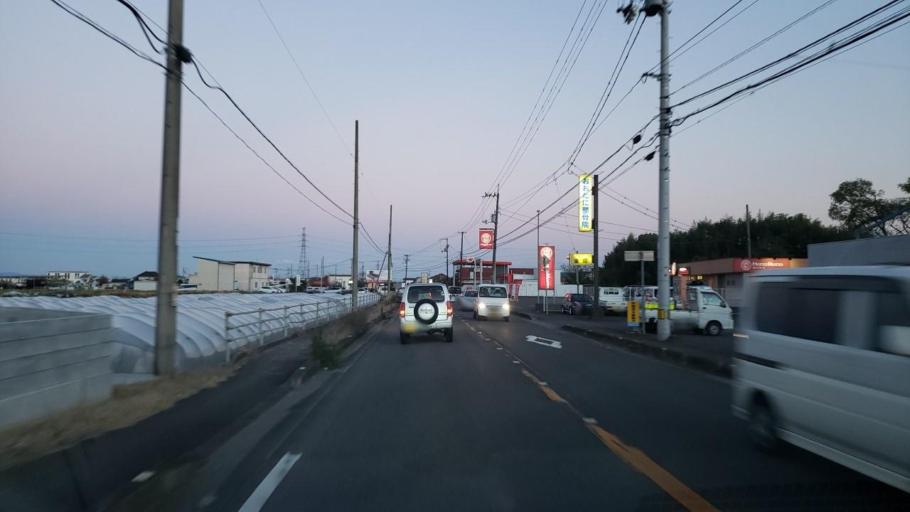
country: JP
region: Tokushima
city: Ishii
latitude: 34.1205
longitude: 134.4381
